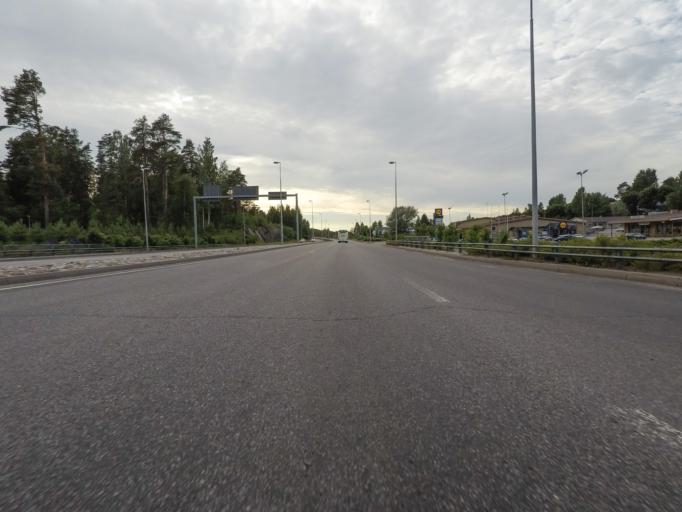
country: FI
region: Southern Savonia
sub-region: Savonlinna
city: Savonlinna
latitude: 61.8682
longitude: 28.9250
